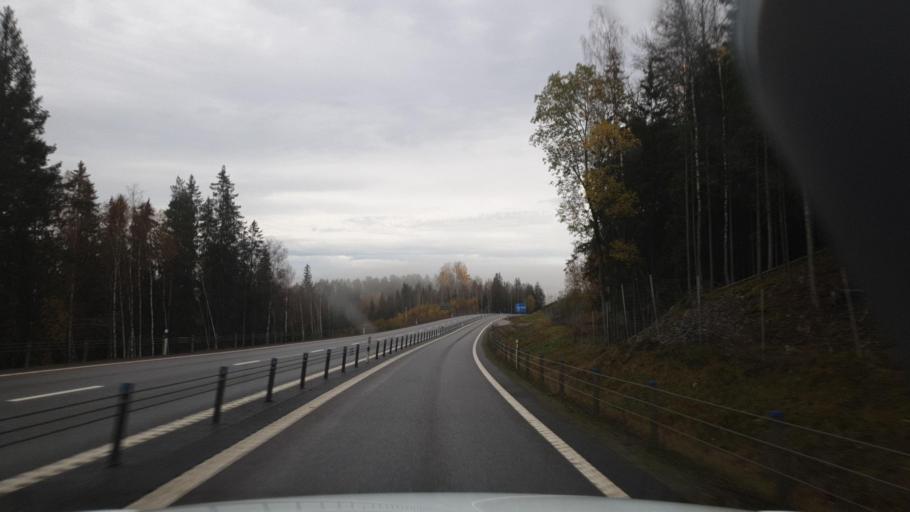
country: SE
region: Vaermland
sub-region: Arvika Kommun
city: Arvika
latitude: 59.6586
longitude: 12.7637
